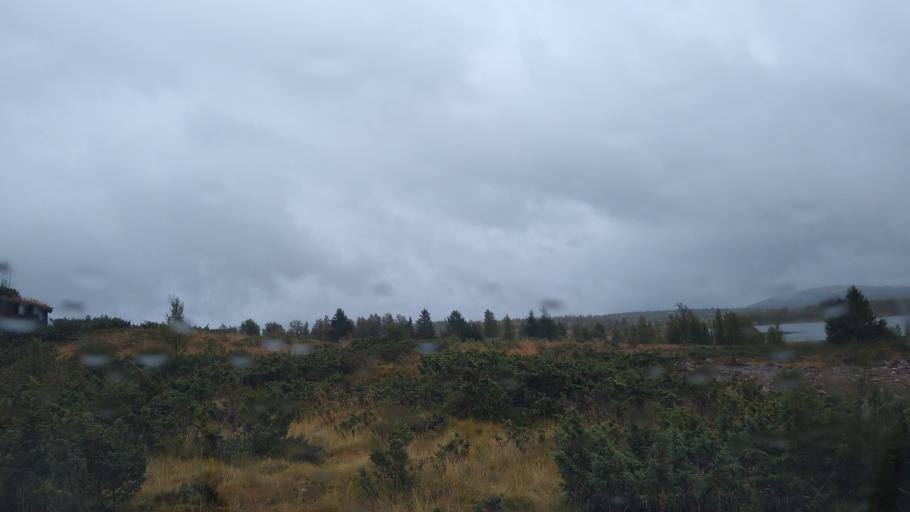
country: NO
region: Oppland
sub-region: Ringebu
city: Ringebu
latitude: 61.6729
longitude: 10.0903
